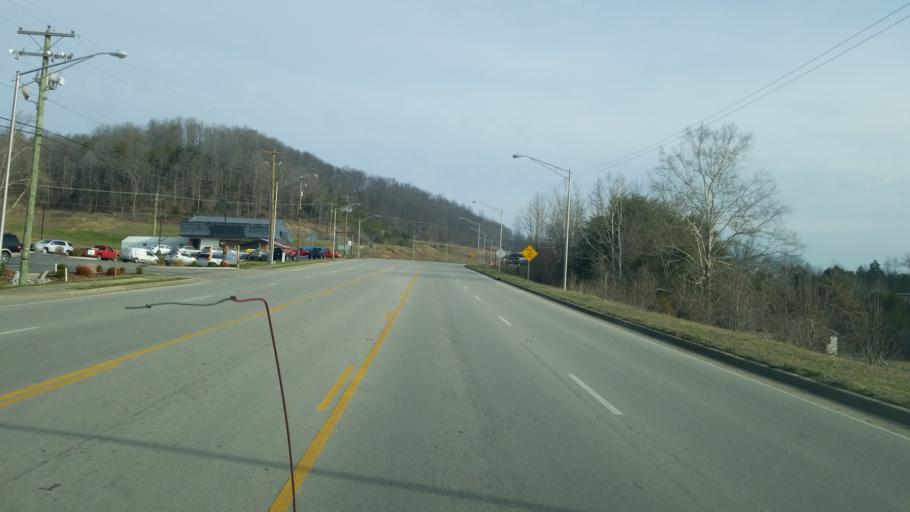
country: US
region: Kentucky
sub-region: Casey County
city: Liberty
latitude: 37.3242
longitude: -84.9241
